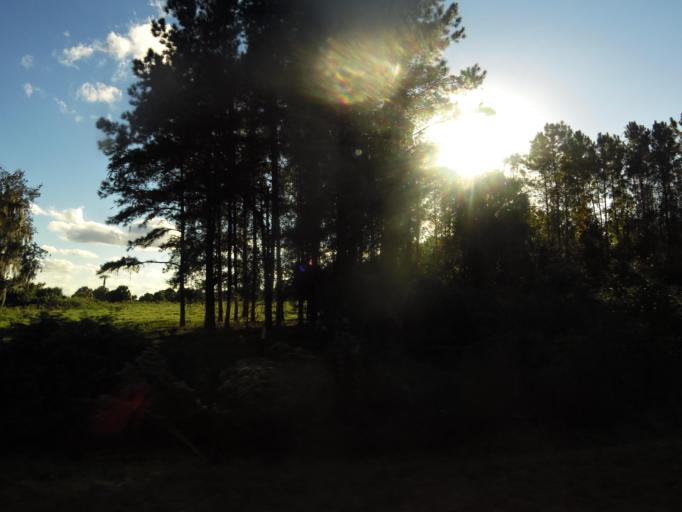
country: US
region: Florida
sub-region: Marion County
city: Citra
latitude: 29.4748
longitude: -82.1577
